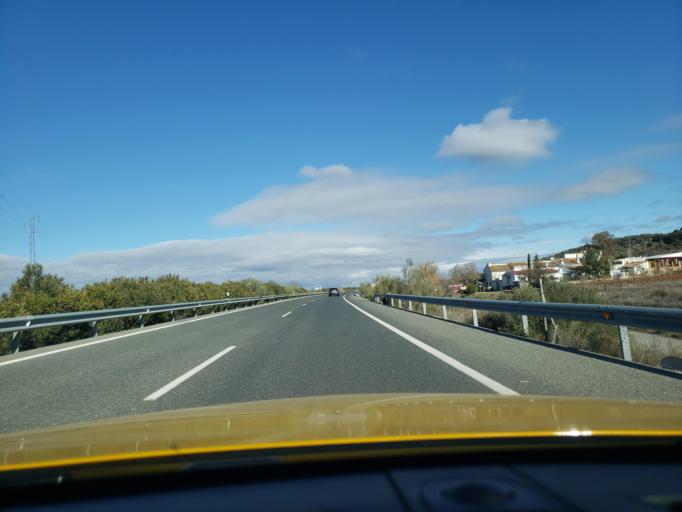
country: ES
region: Andalusia
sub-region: Provincia de Malaga
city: Archidona
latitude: 37.0985
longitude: -4.3152
